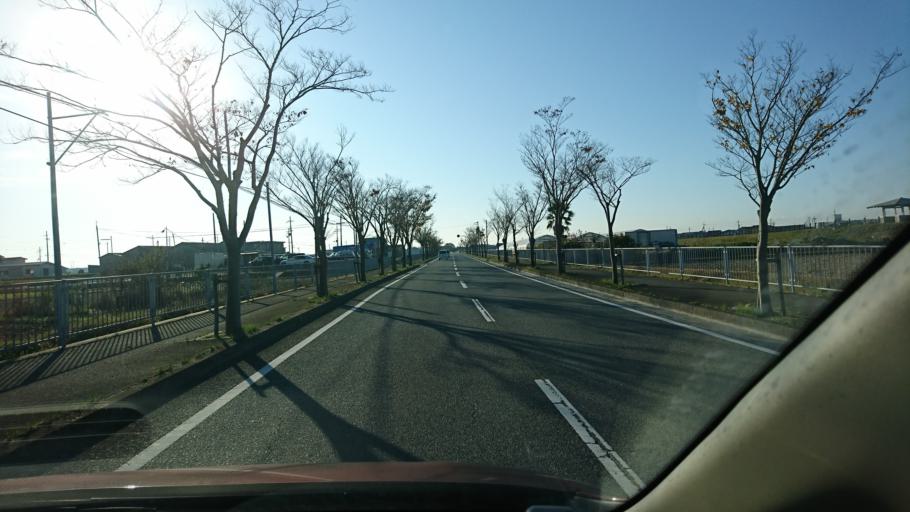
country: JP
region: Hyogo
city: Miki
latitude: 34.7698
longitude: 134.9112
